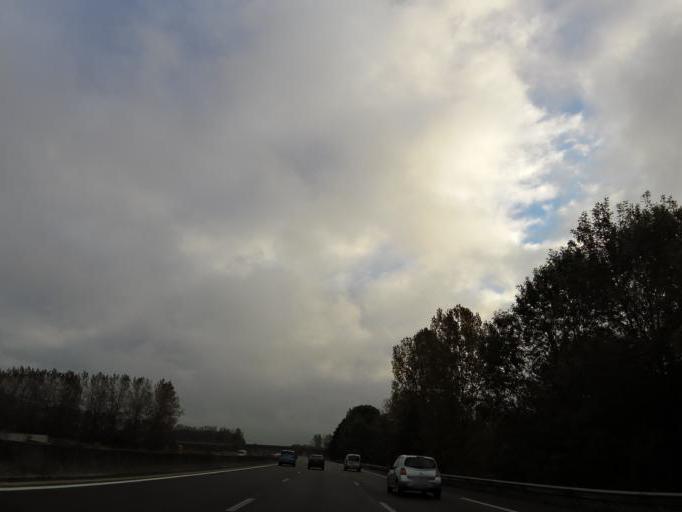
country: FR
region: Ile-de-France
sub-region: Departement de Seine-et-Marne
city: Bailly-Romainvilliers
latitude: 48.8378
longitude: 2.8148
